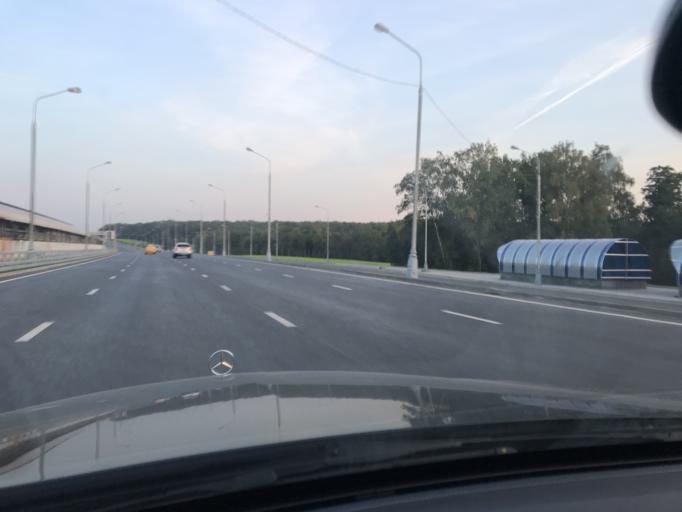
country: RU
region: Moskovskaya
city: Mosrentgen
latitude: 55.5909
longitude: 37.4229
